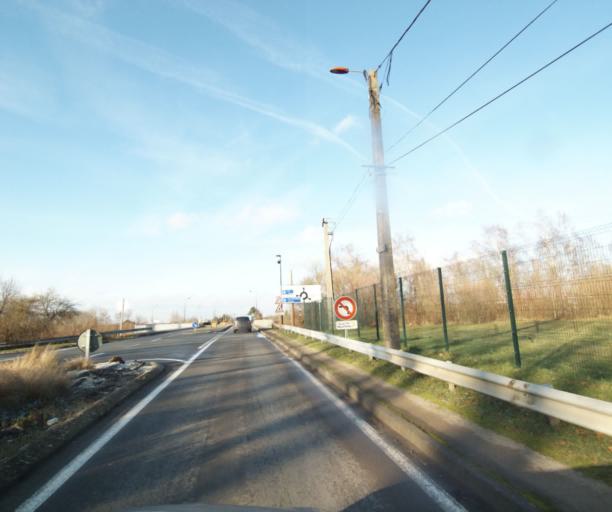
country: FR
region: Nord-Pas-de-Calais
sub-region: Departement du Nord
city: Marly
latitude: 50.3357
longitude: 3.5552
